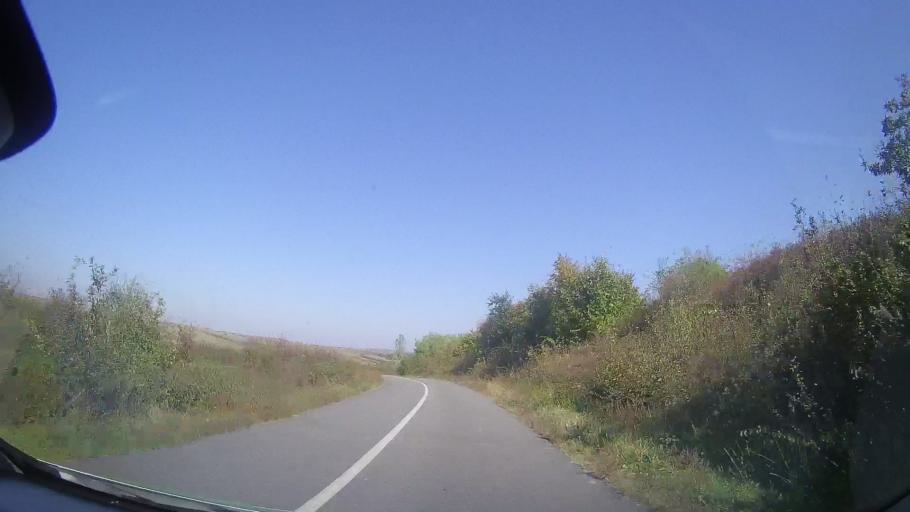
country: RO
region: Timis
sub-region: Comuna Balint
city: Balint
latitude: 45.8318
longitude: 21.8552
